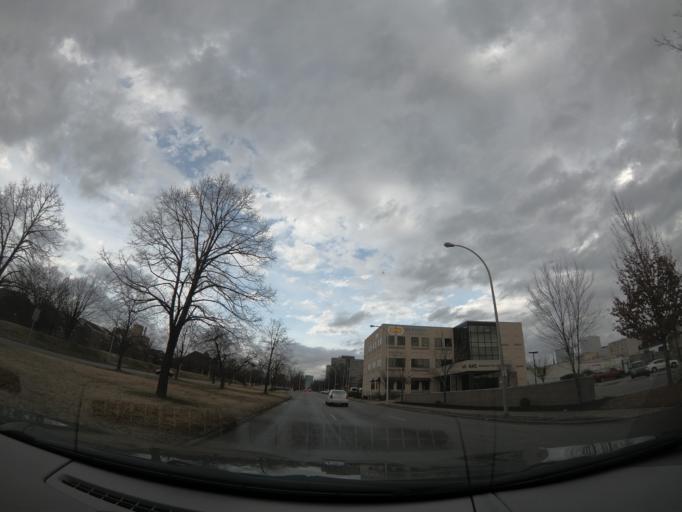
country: US
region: Kentucky
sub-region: Jefferson County
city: Louisville
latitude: 38.2475
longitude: -85.7663
